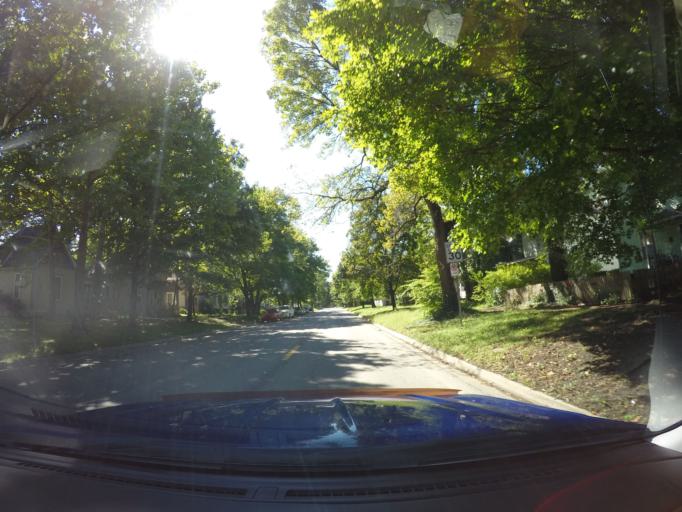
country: US
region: Kansas
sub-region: Douglas County
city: Lawrence
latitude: 38.9635
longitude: -95.2324
